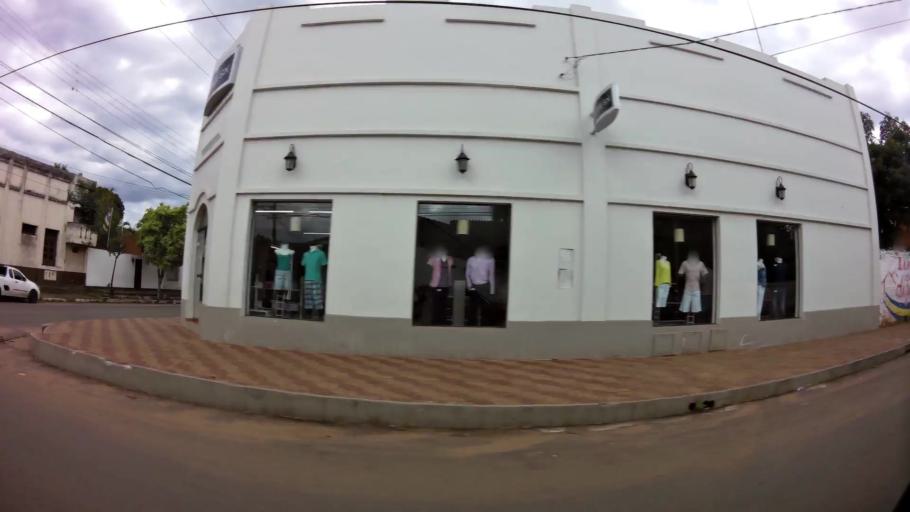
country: PY
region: Central
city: San Lorenzo
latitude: -25.2653
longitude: -57.4918
